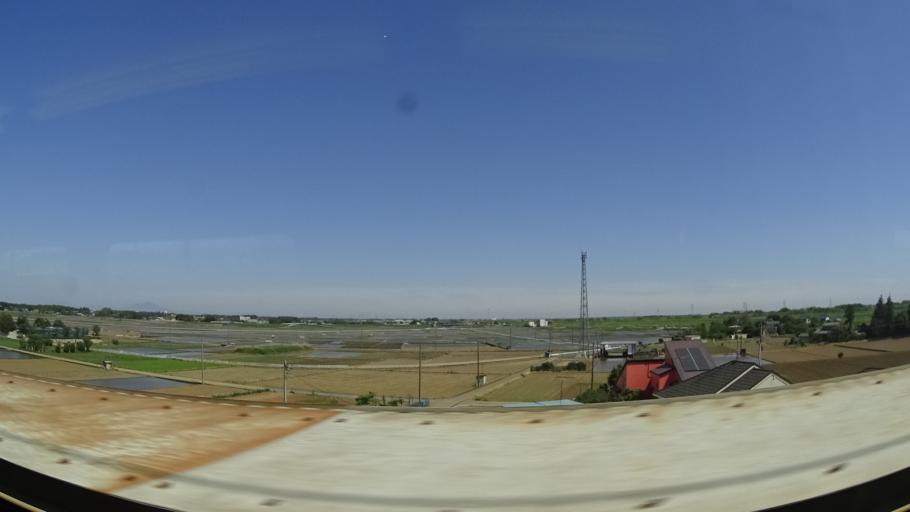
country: JP
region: Saitama
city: Kurihashi
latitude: 36.1408
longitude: 139.7223
